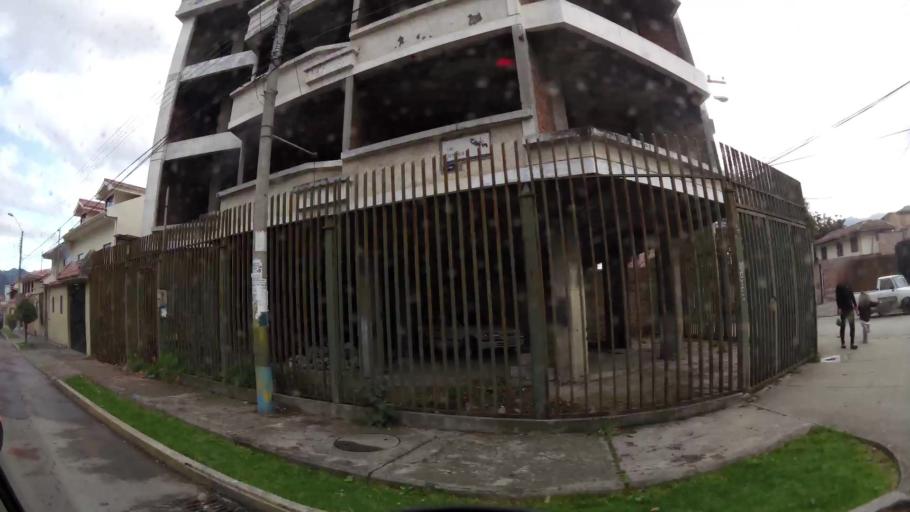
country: EC
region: Azuay
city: Cuenca
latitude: -2.8983
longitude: -79.0244
